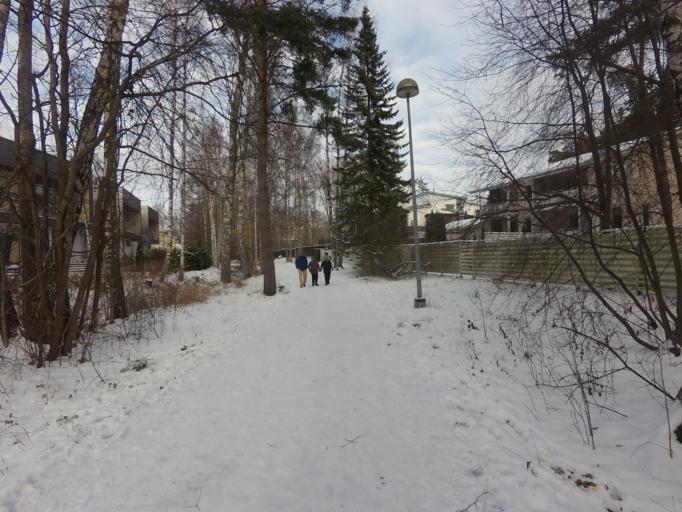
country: FI
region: Uusimaa
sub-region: Helsinki
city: Koukkuniemi
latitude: 60.1492
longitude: 24.7425
